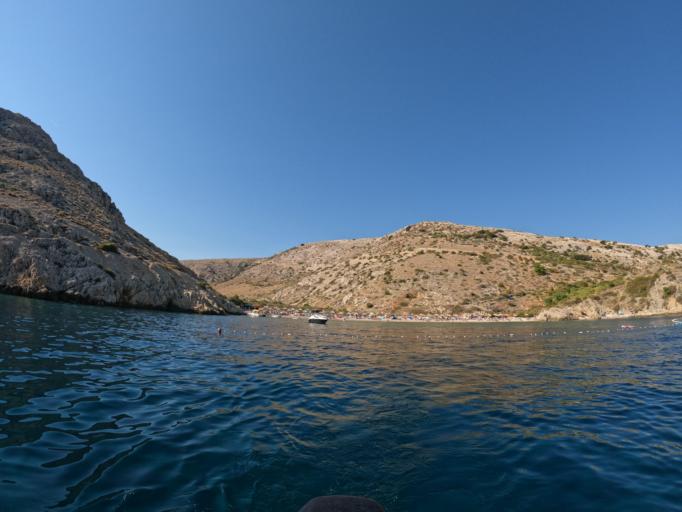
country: HR
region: Primorsko-Goranska
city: Punat
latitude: 44.9659
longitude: 14.6623
